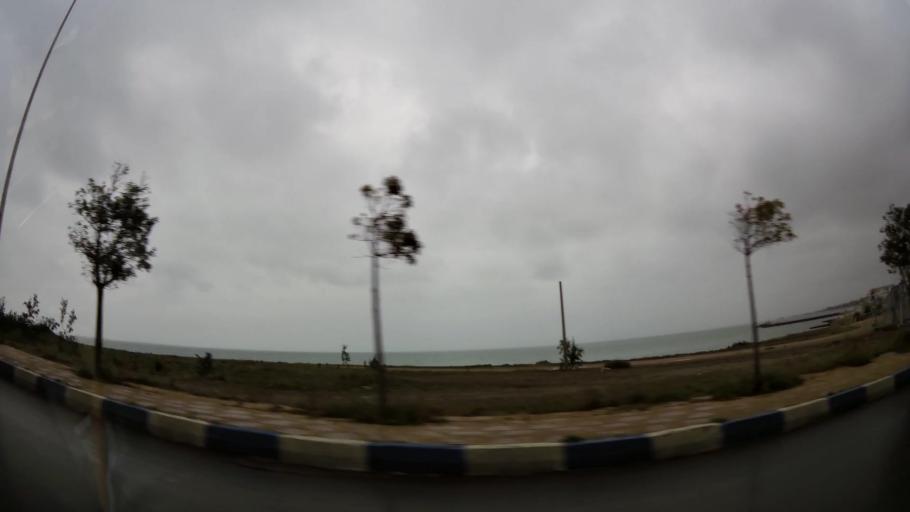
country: MA
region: Oriental
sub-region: Nador
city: Nador
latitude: 35.1887
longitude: -2.9258
